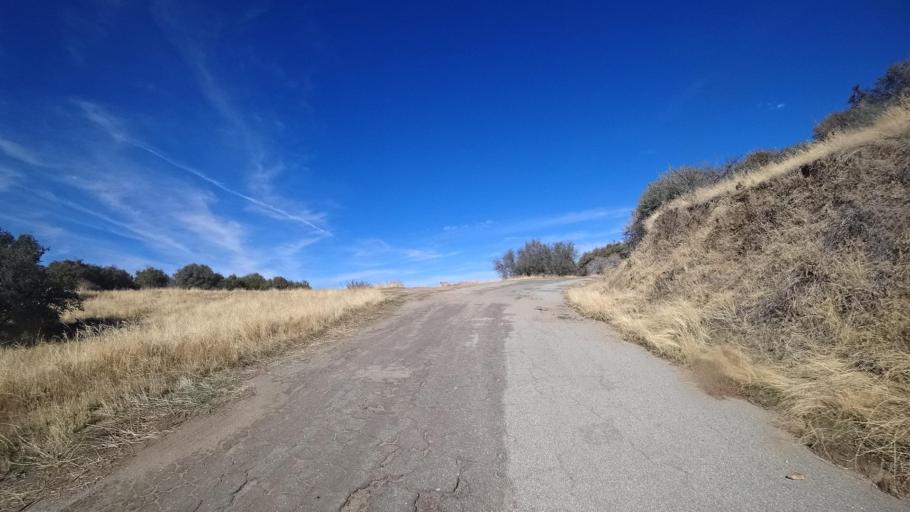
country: US
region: California
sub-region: Kern County
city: Bodfish
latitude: 35.4596
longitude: -118.6560
